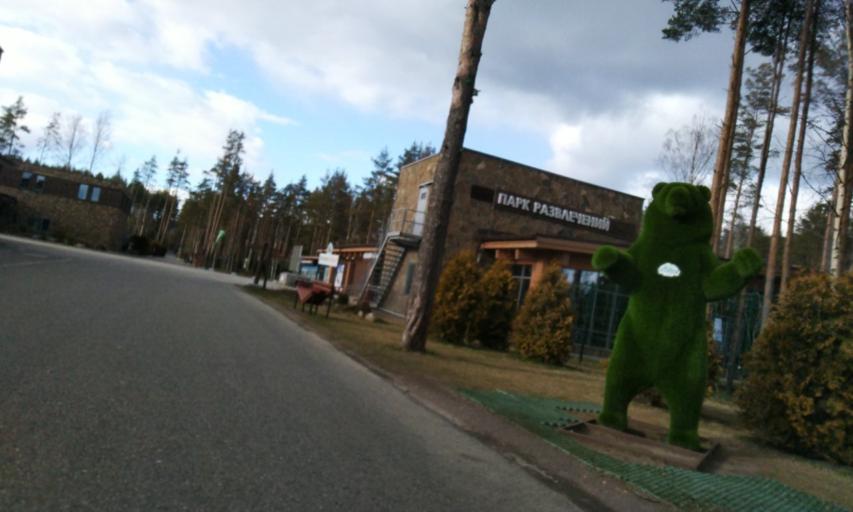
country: RU
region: Leningrad
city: Novoye Devyatkino
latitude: 60.1272
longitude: 30.4462
